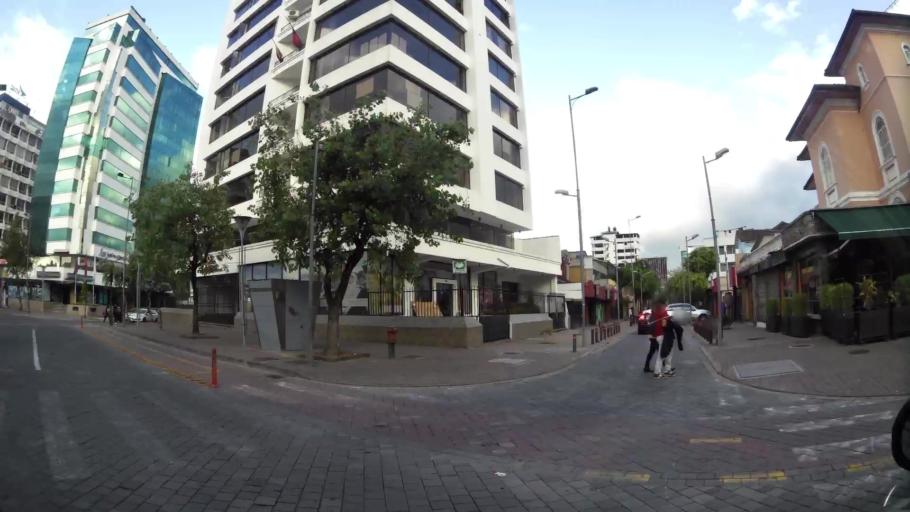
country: EC
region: Pichincha
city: Quito
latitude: -0.2012
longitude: -78.4916
